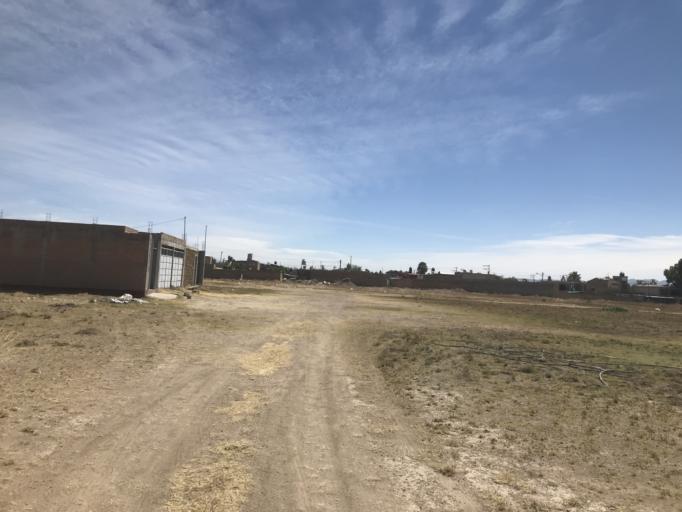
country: MX
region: Durango
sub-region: Durango
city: Sebastian Lerdo de Tejada
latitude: 23.9771
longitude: -104.6540
